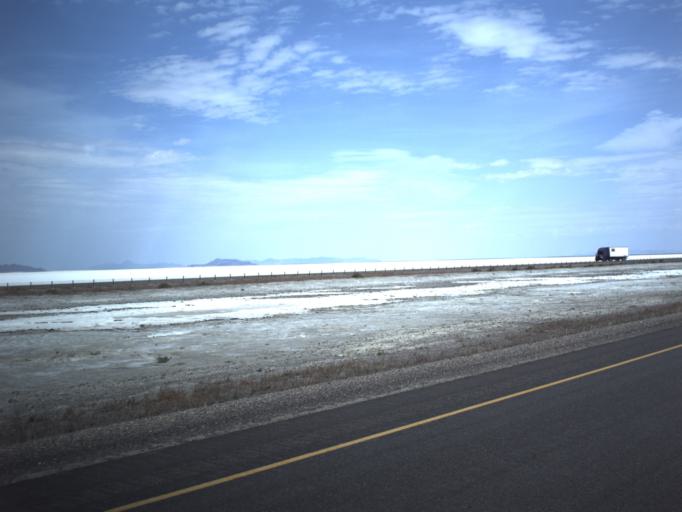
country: US
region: Utah
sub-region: Tooele County
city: Wendover
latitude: 40.7391
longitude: -113.8840
